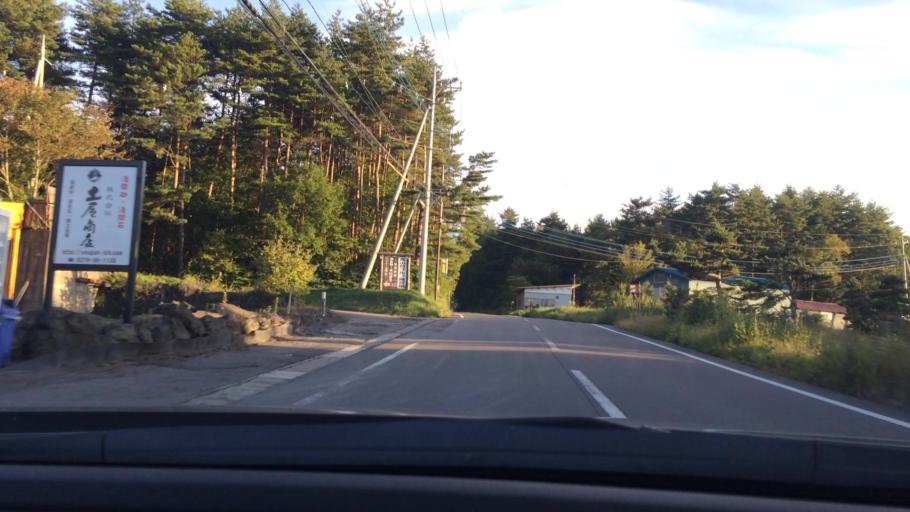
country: JP
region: Nagano
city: Komoro
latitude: 36.4944
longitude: 138.5111
